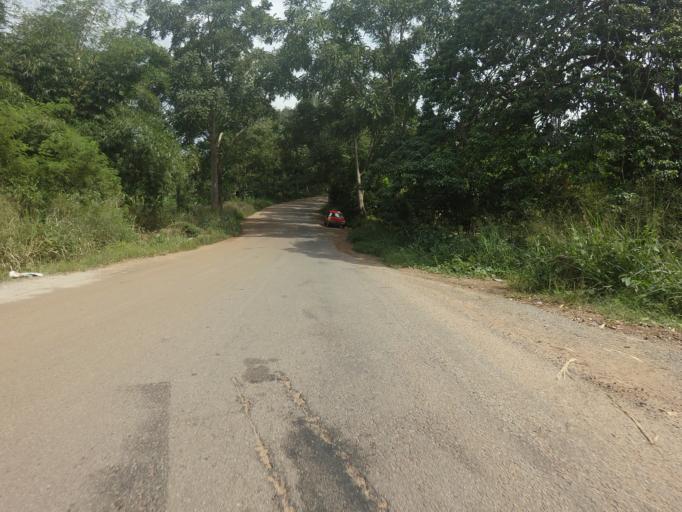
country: GH
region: Eastern
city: Aburi
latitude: 5.9535
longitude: -0.2140
